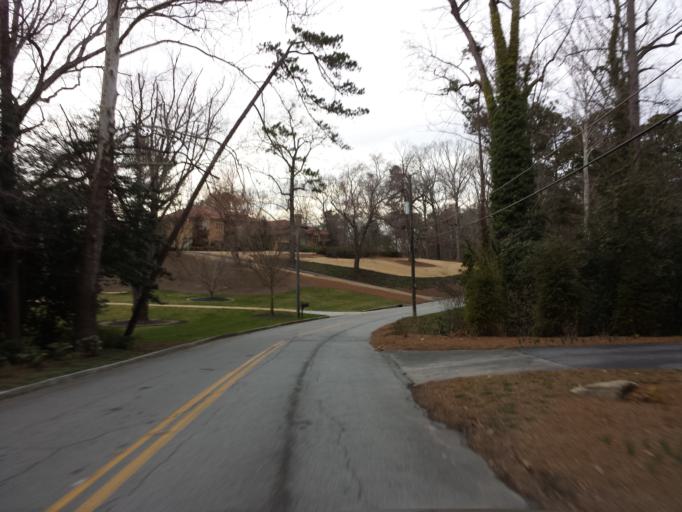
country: US
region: Georgia
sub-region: Cobb County
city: Vinings
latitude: 33.8722
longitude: -84.4341
